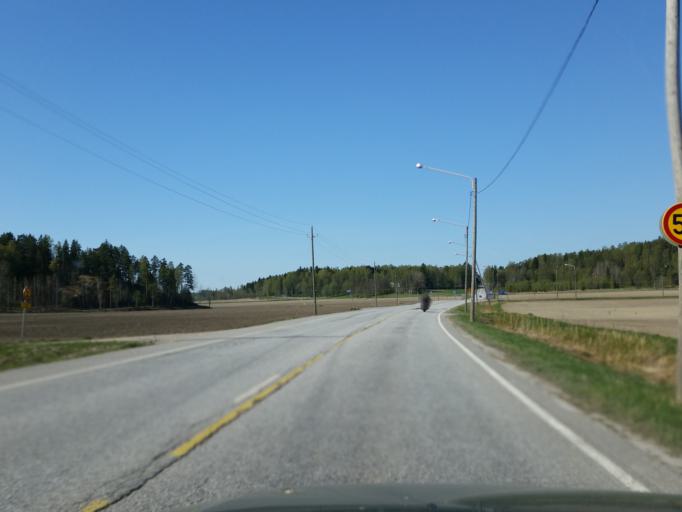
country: FI
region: Uusimaa
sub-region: Helsinki
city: Siuntio
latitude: 60.1740
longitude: 24.2119
